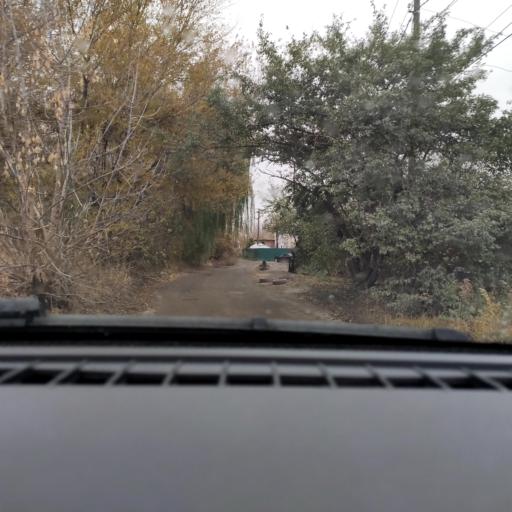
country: RU
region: Voronezj
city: Voronezh
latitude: 51.6606
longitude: 39.2707
